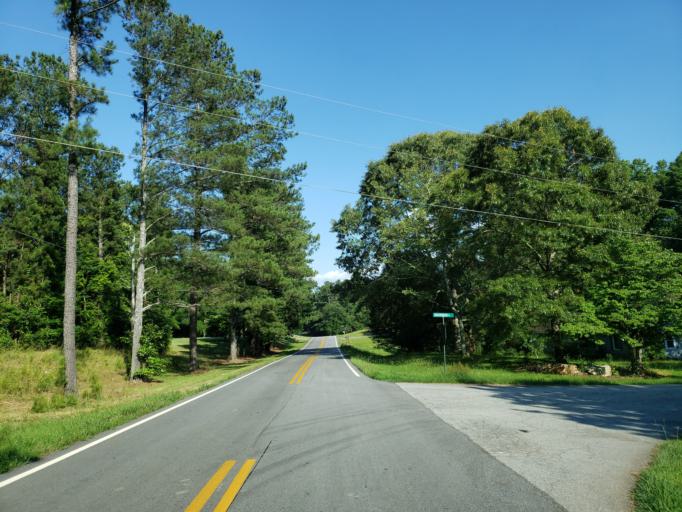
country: US
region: Georgia
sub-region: Haralson County
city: Bremen
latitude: 33.7070
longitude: -85.1131
